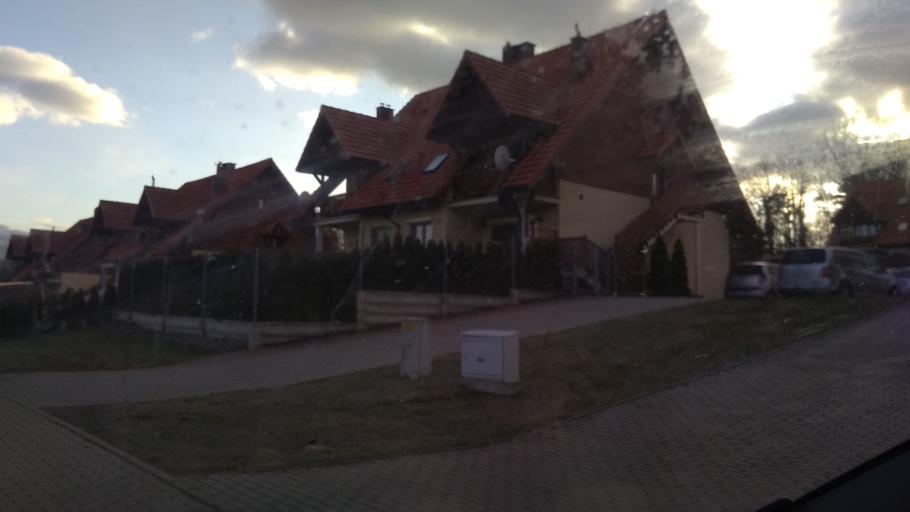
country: PL
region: Lower Silesian Voivodeship
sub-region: Jelenia Gora
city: Cieplice Slaskie Zdroj
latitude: 50.8542
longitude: 15.7151
